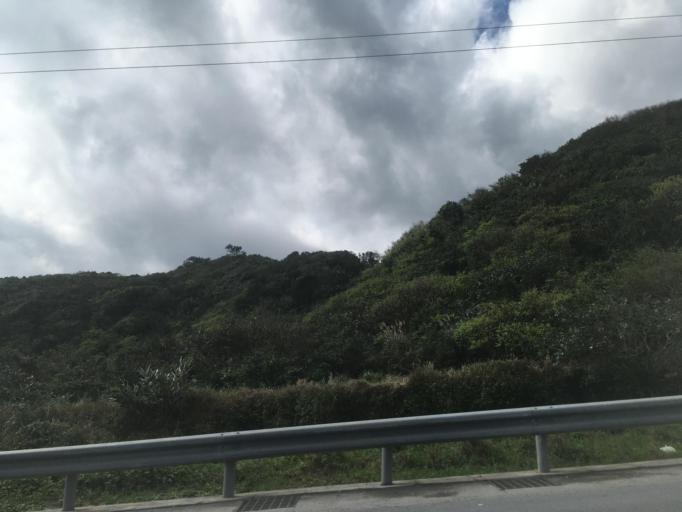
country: TW
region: Taiwan
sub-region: Keelung
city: Keelung
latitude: 25.0202
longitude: 121.9559
